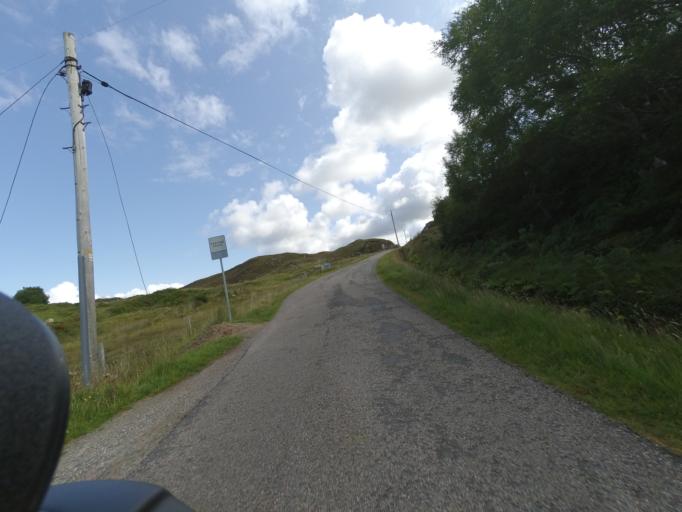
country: GB
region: Scotland
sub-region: Highland
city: Ullapool
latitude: 58.2430
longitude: -5.1891
